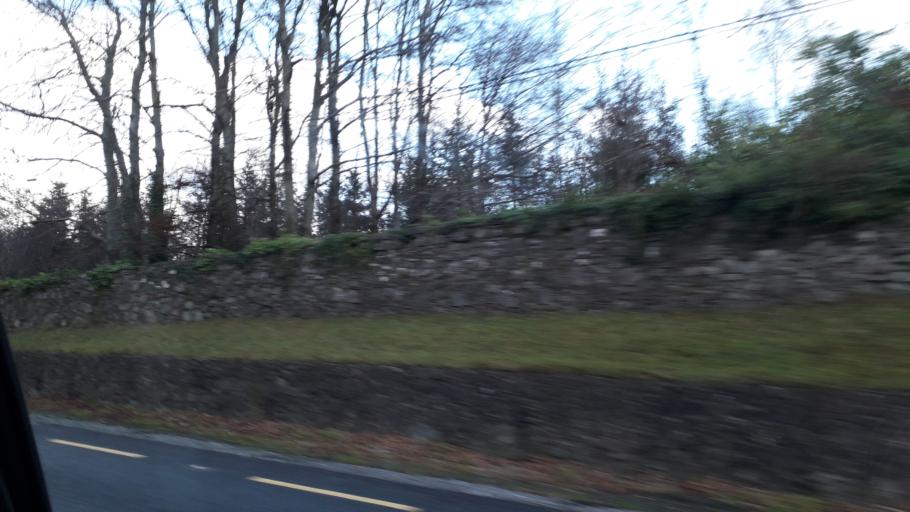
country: IE
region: Leinster
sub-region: Lu
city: Tullyallen
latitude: 53.7832
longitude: -6.4877
